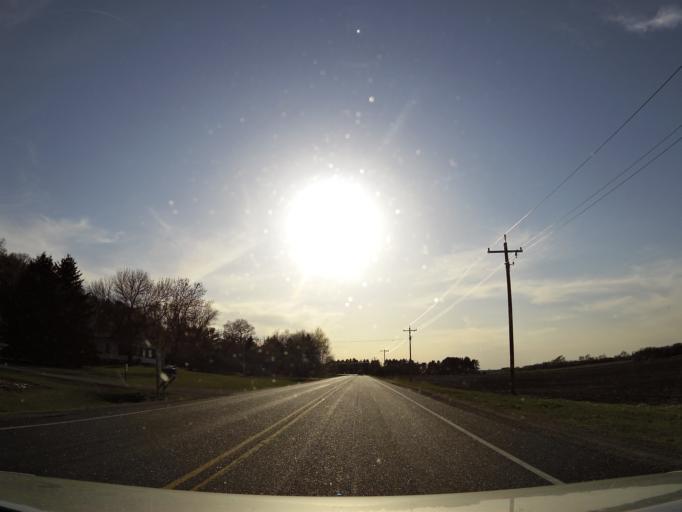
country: US
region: Wisconsin
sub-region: Pierce County
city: River Falls
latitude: 44.8257
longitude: -92.6863
